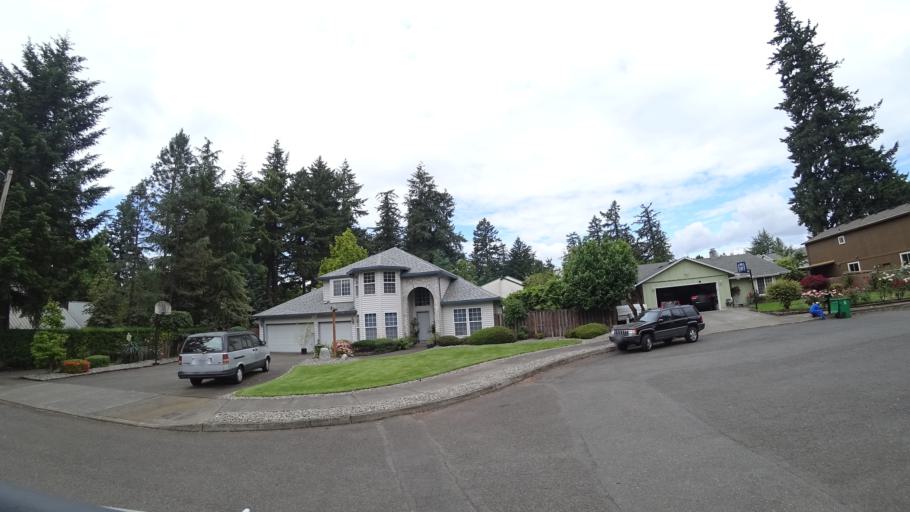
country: US
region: Oregon
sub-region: Multnomah County
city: Lents
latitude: 45.5001
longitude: -122.5299
